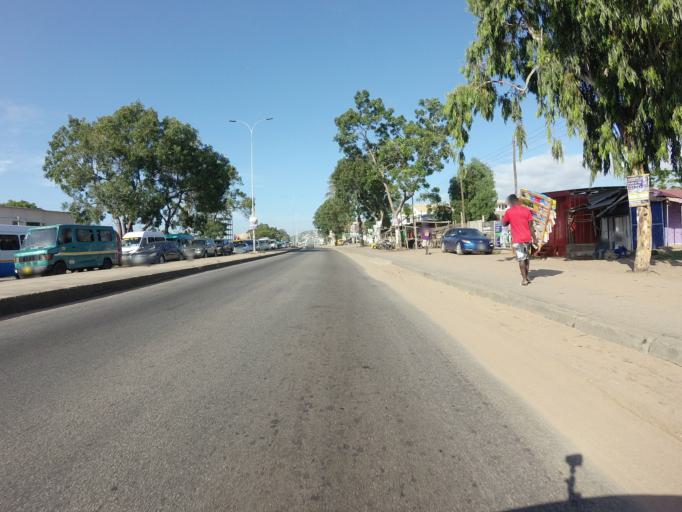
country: GH
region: Greater Accra
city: Gbawe
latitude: 5.5778
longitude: -0.2719
